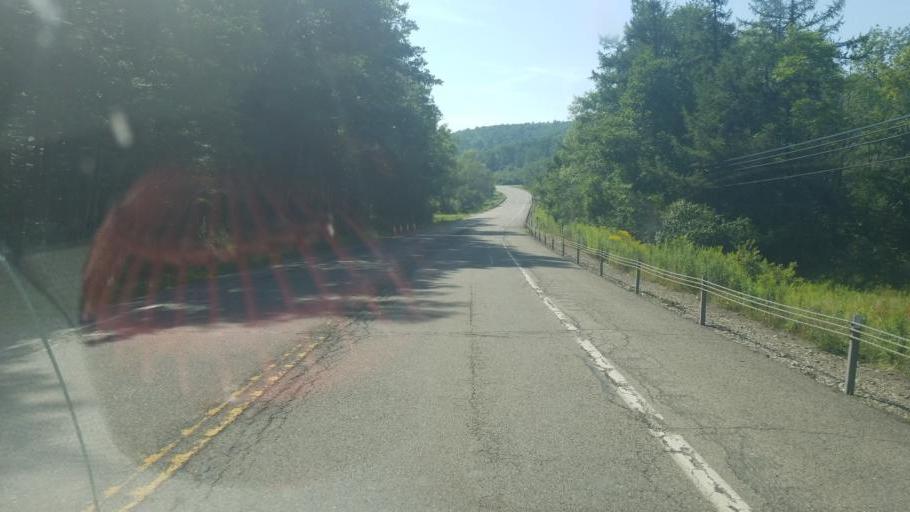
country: US
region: New York
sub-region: Allegany County
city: Wellsville
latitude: 42.1033
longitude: -78.0312
